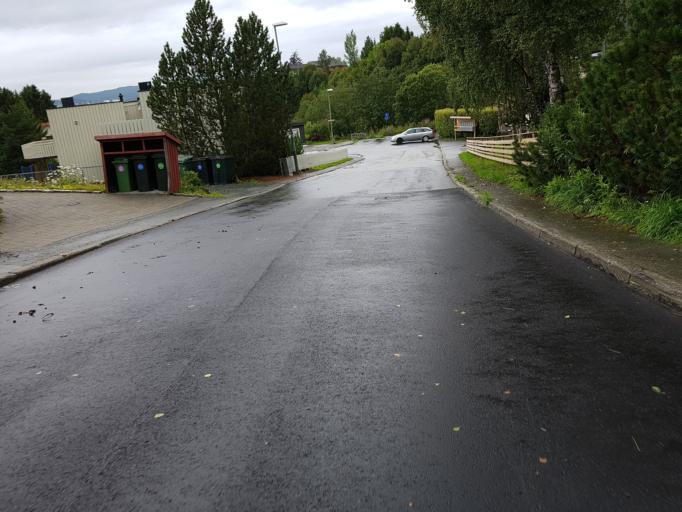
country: NO
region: Sor-Trondelag
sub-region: Trondheim
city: Trondheim
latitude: 63.3890
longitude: 10.4170
